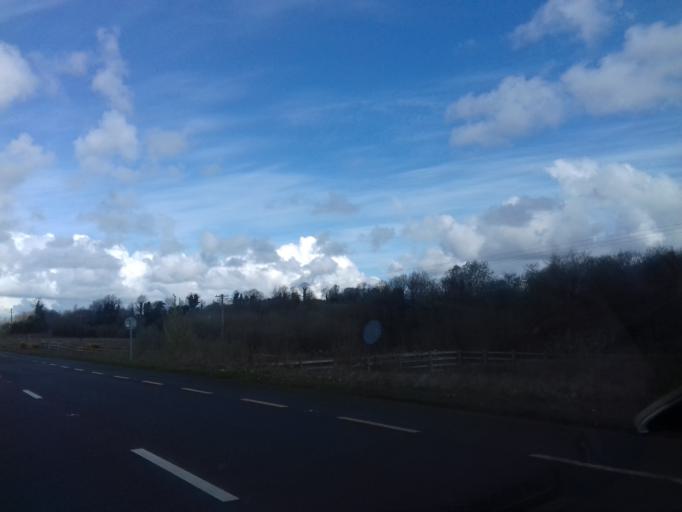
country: IE
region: Ulster
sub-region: An Cabhan
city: Belturbet
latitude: 54.0719
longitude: -7.4112
